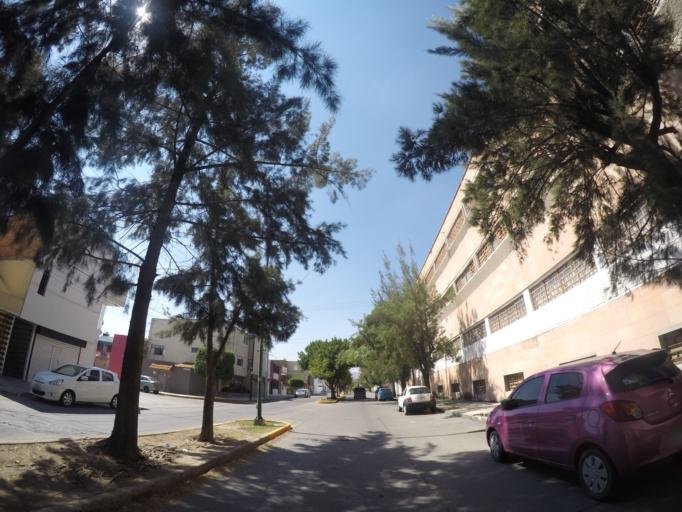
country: MX
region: San Luis Potosi
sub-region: San Luis Potosi
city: San Luis Potosi
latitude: 22.1438
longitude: -101.0122
